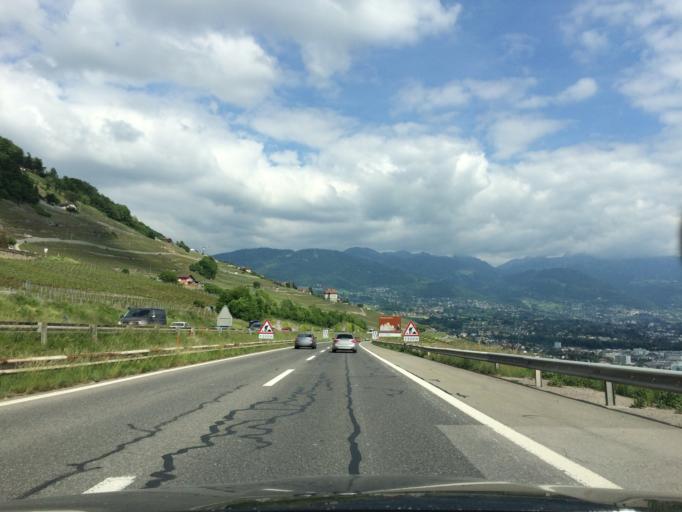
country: CH
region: Vaud
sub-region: Riviera-Pays-d'Enhaut District
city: Chardonne
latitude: 46.4751
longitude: 6.8110
